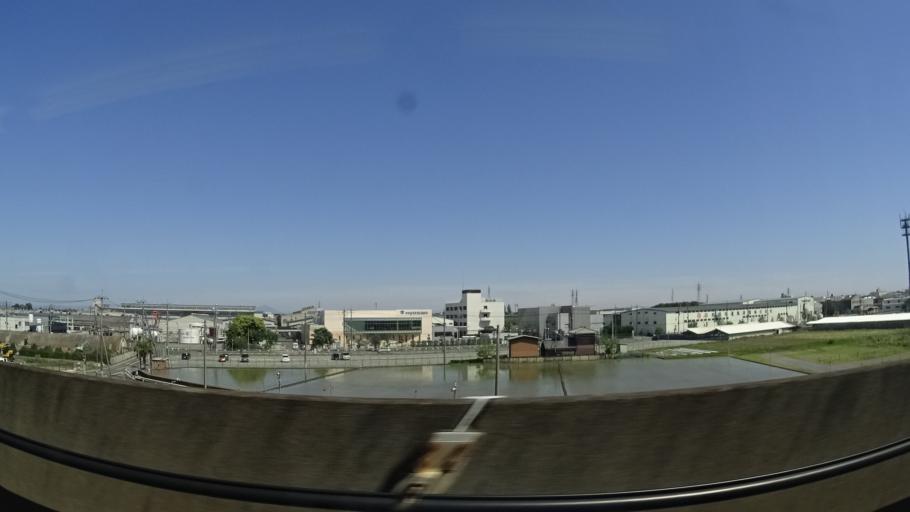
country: JP
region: Ibaraki
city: Koga
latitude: 36.2015
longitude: 139.7478
